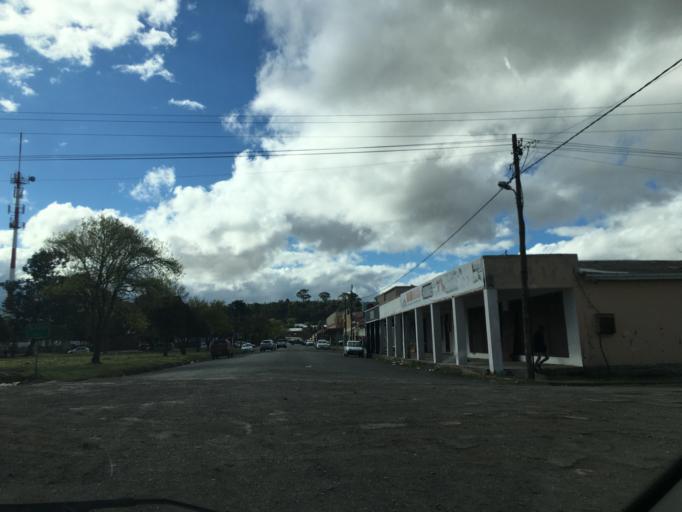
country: ZA
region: Eastern Cape
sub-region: Chris Hani District Municipality
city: Elliot
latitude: -31.3347
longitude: 27.8516
